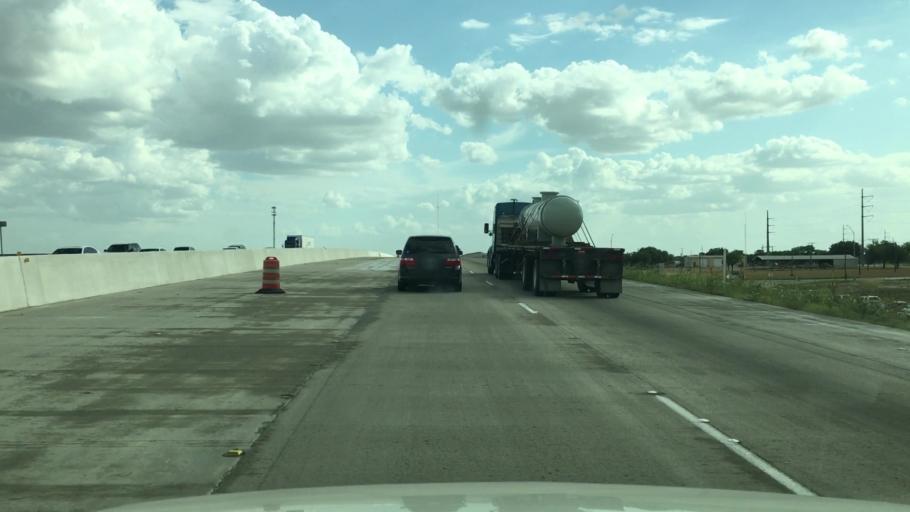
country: US
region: Texas
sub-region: McLennan County
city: Bruceville-Eddy
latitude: 31.3090
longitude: -97.2438
